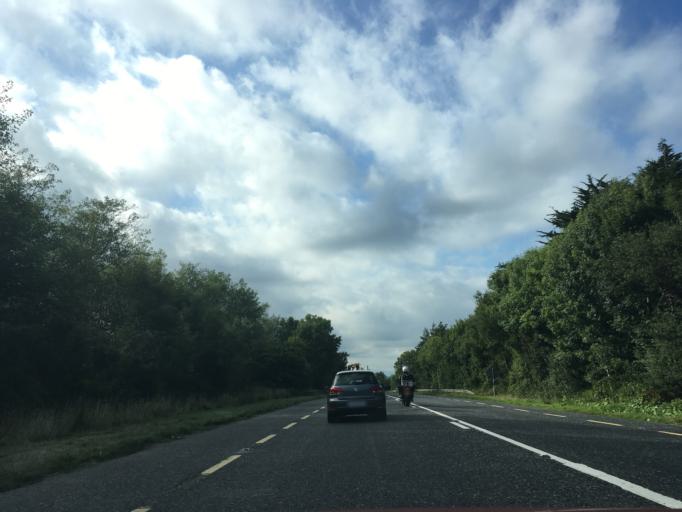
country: IE
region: Leinster
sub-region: Loch Garman
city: Loch Garman
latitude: 52.3265
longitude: -6.5046
